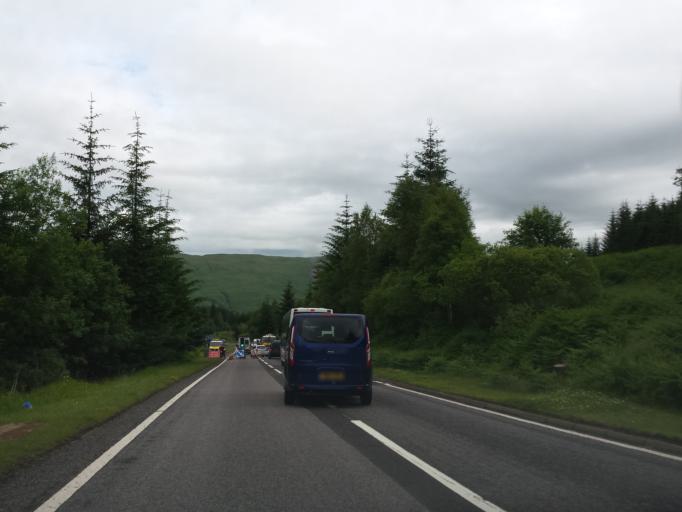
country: GB
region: Scotland
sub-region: Stirling
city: Callander
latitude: 56.4318
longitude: -4.3413
